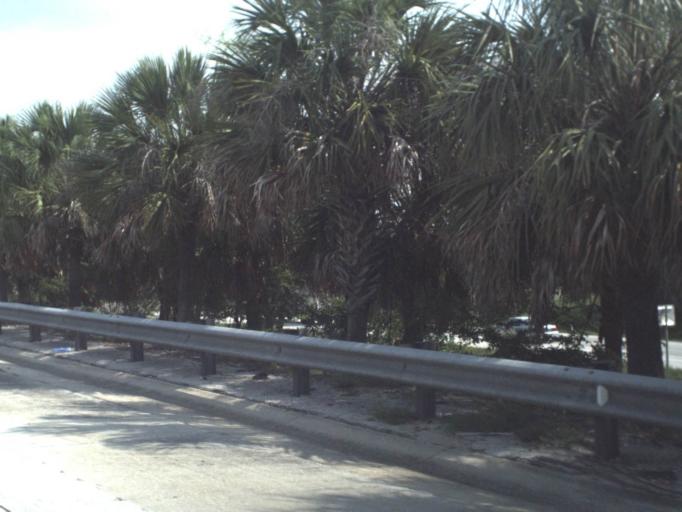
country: US
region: Florida
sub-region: Saint Johns County
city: Fruit Cove
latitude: 30.2195
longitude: -81.5701
